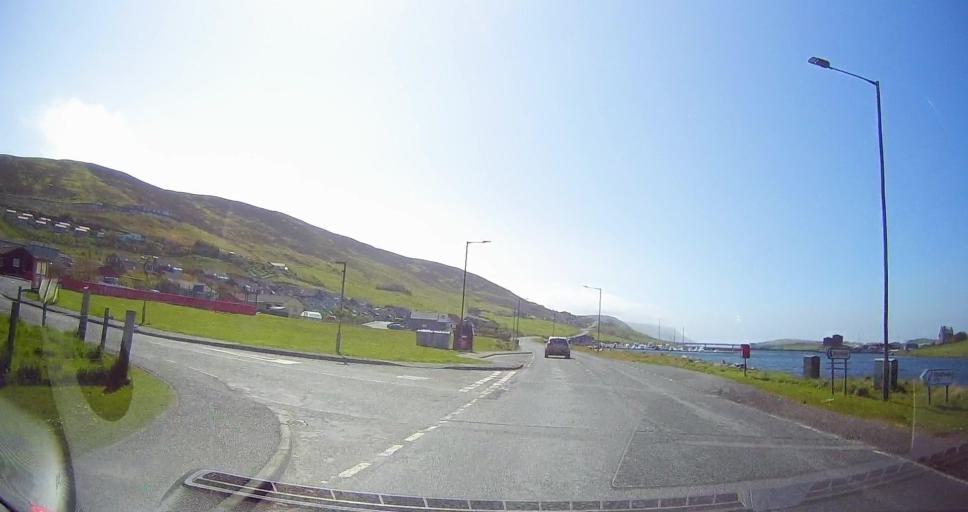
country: GB
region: Scotland
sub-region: Shetland Islands
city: Lerwick
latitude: 60.1404
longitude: -1.2670
